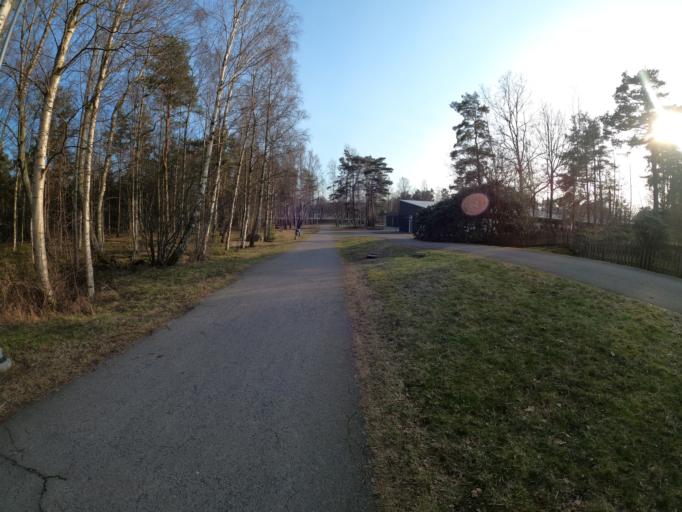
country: SE
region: Vaestra Goetaland
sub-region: Harryda Kommun
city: Molnlycke
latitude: 57.6519
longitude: 12.1205
